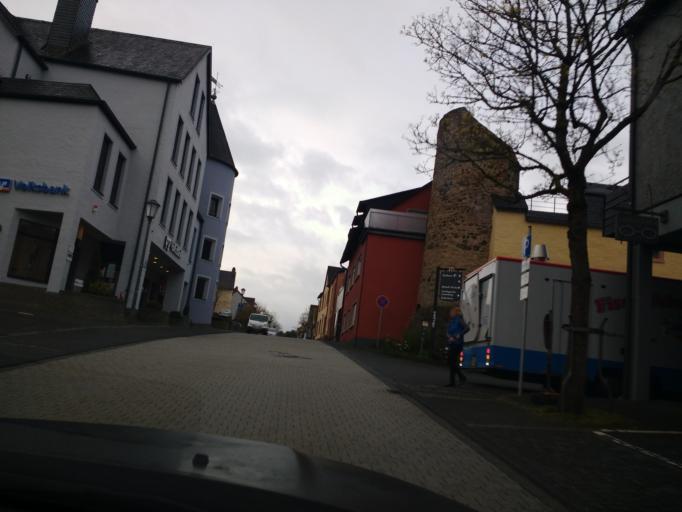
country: DE
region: Rheinland-Pfalz
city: Hillesheim
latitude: 50.2910
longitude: 6.6719
